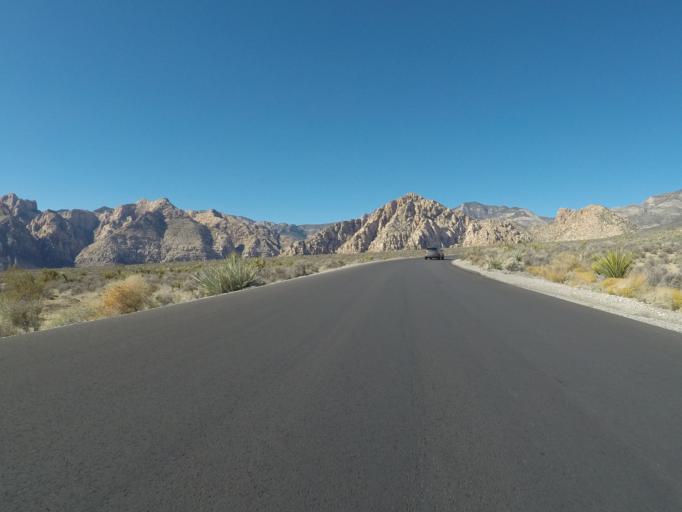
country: US
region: Nevada
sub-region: Clark County
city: Summerlin South
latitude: 36.1635
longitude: -115.4625
